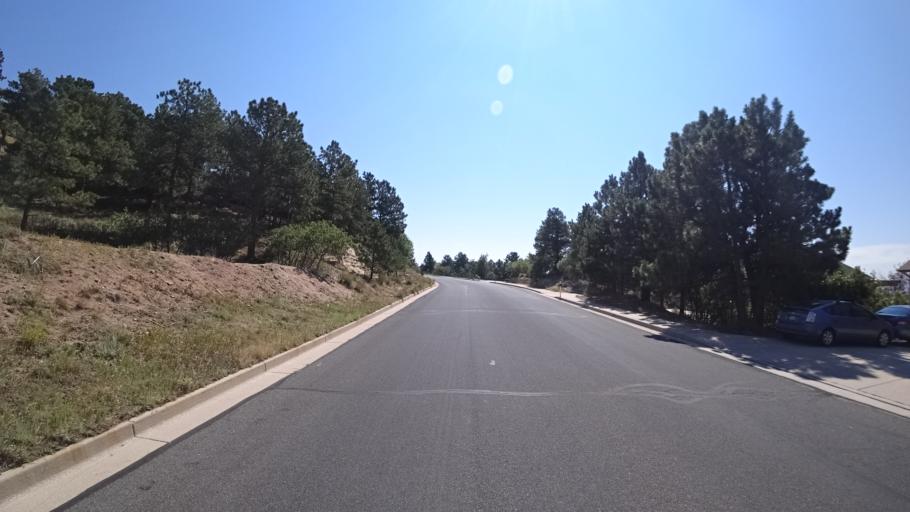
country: US
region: Colorado
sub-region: El Paso County
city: Air Force Academy
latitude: 38.9297
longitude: -104.8592
